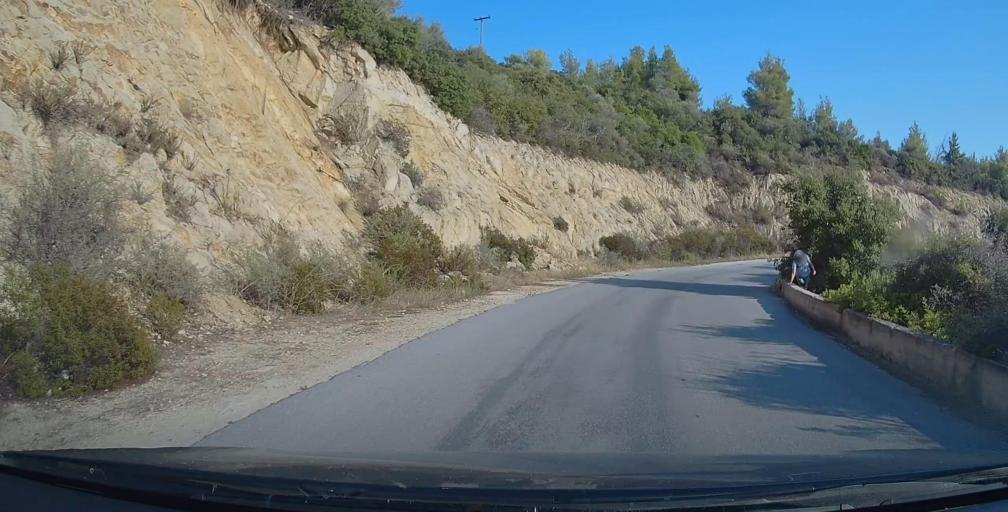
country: GR
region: Central Macedonia
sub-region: Nomos Chalkidikis
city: Sykia
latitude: 39.9937
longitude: 23.8928
